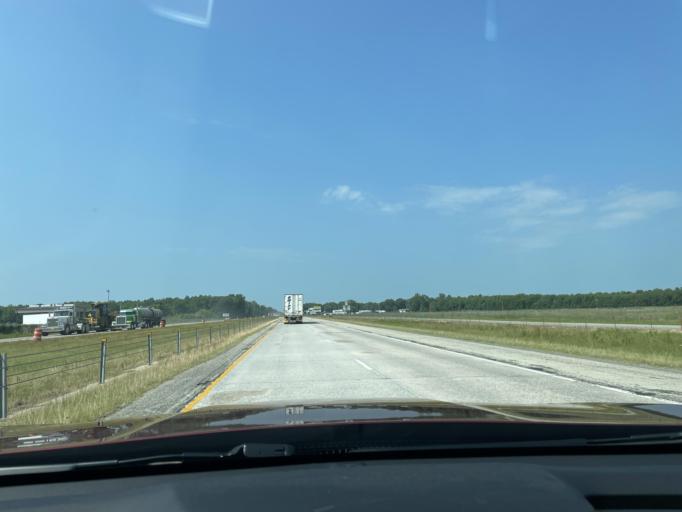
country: US
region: Arkansas
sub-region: White County
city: Searcy
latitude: 35.1996
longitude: -91.7375
